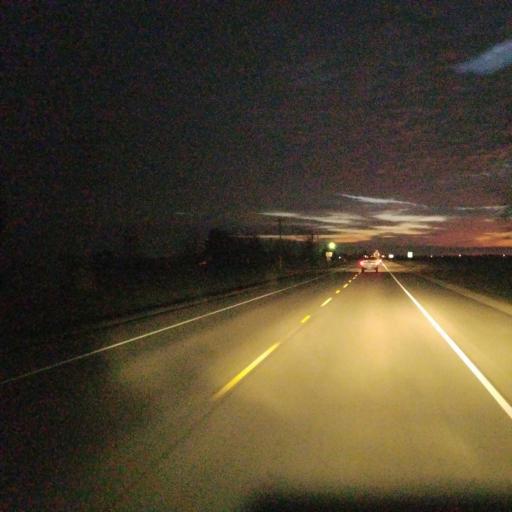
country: US
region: Illinois
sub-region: Peoria County
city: Hanna City
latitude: 40.6975
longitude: -89.8806
